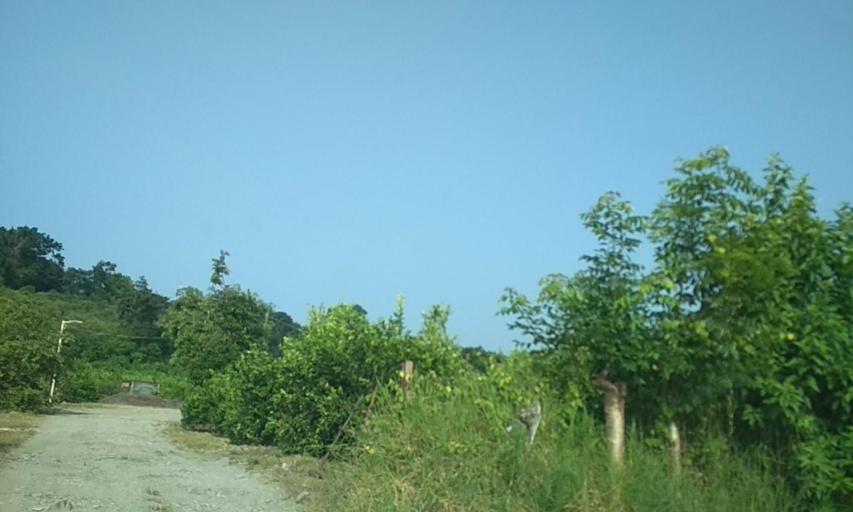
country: MX
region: Veracruz
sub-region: Misantla
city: La Defensa
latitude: 20.0502
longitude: -96.9813
